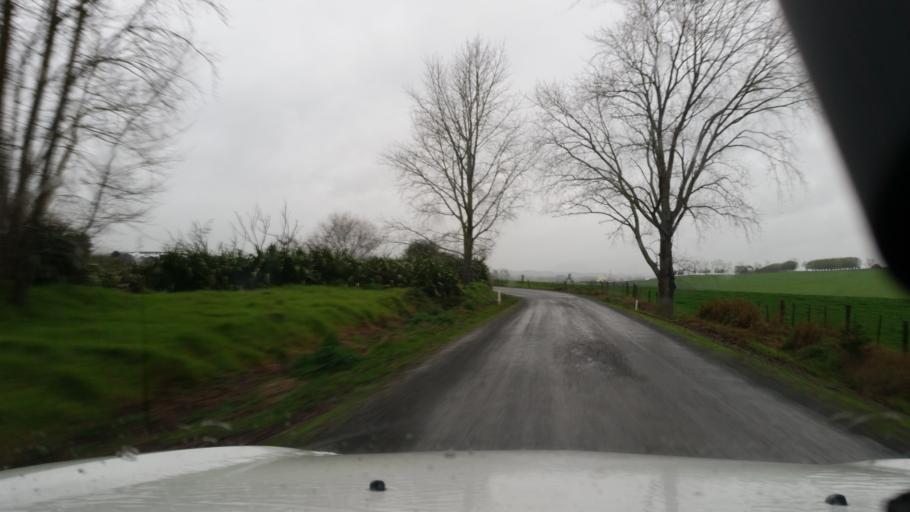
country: NZ
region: Northland
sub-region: Whangarei
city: Maungatapere
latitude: -35.7353
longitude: 174.0843
